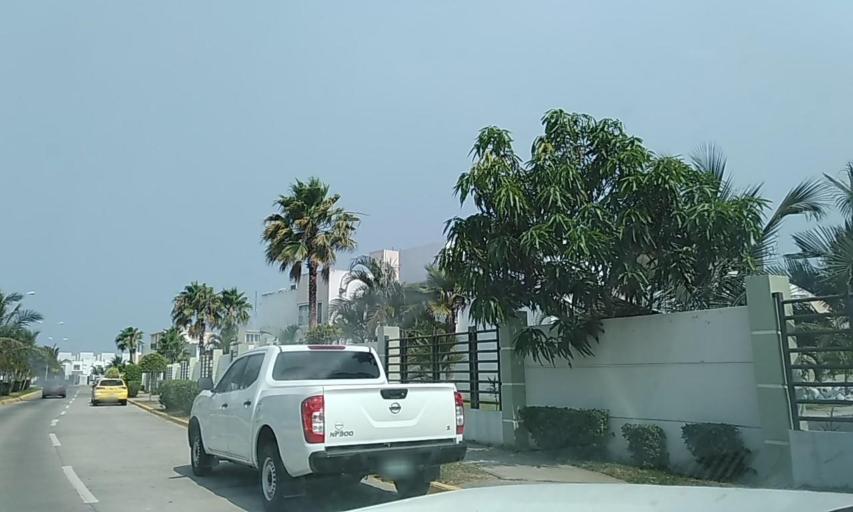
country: MX
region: Veracruz
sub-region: Veracruz
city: Hacienda Sotavento
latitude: 19.1328
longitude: -96.1700
